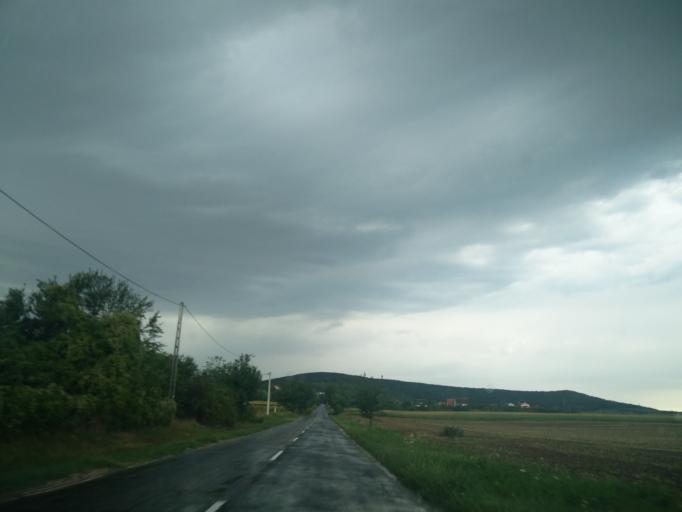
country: HU
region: Fejer
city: Velence
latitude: 47.2534
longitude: 18.6272
